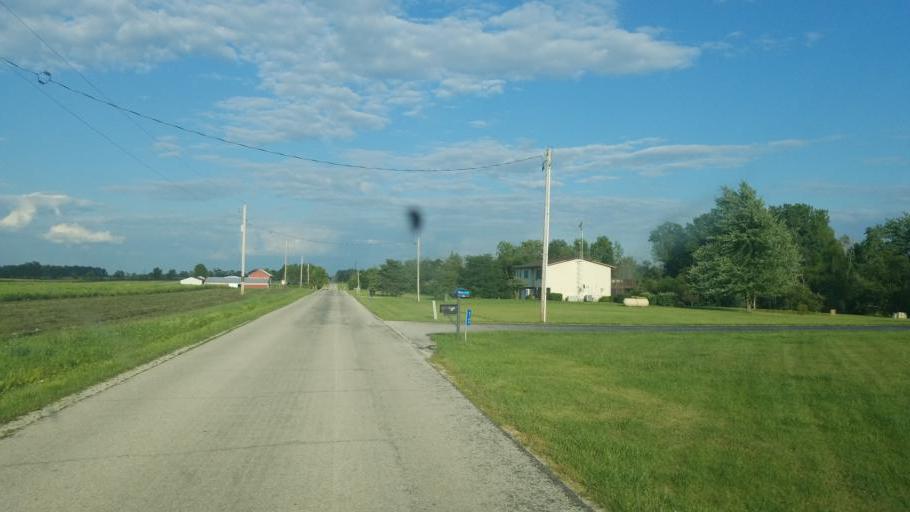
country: US
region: Ohio
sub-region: Seneca County
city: Tiffin
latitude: 41.1097
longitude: -83.0521
